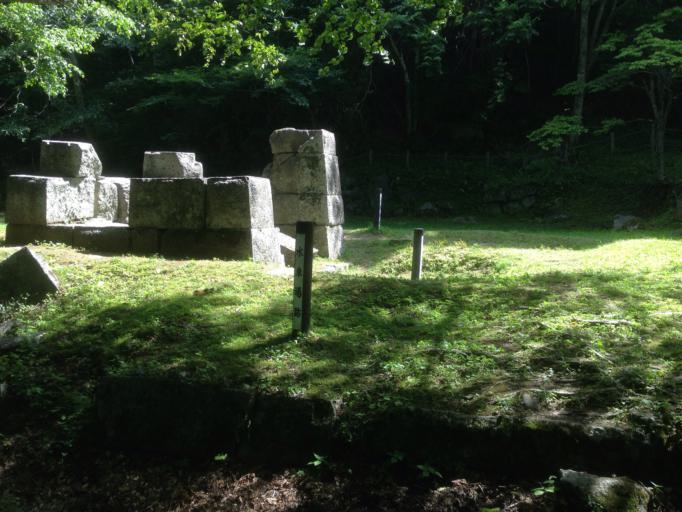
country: JP
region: Iwate
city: Tono
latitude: 39.3427
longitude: 141.6826
